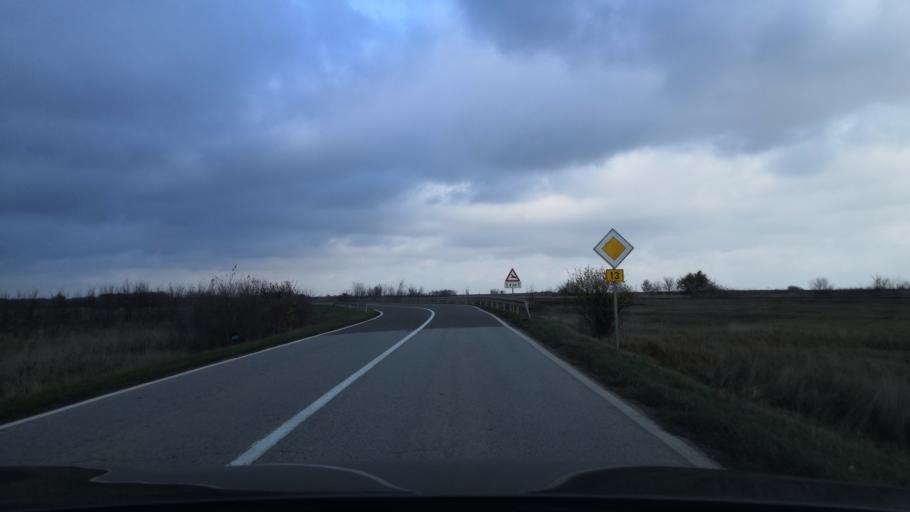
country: RS
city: Sanad
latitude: 45.9857
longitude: 20.1108
